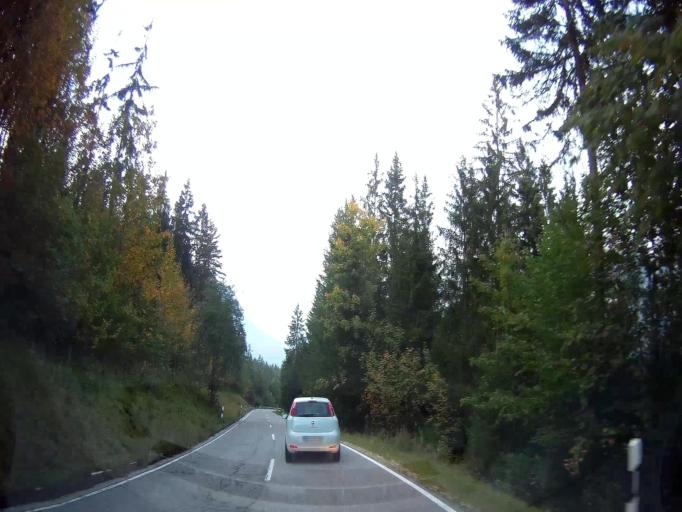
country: DE
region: Bavaria
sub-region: Upper Bavaria
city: Bischofswiesen
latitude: 47.6502
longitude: 12.9448
